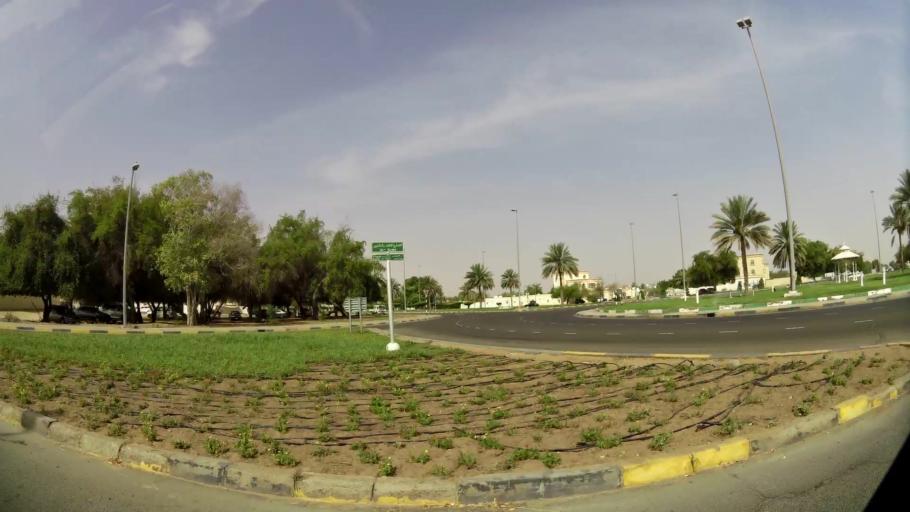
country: AE
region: Abu Dhabi
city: Al Ain
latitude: 24.1505
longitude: 55.6958
